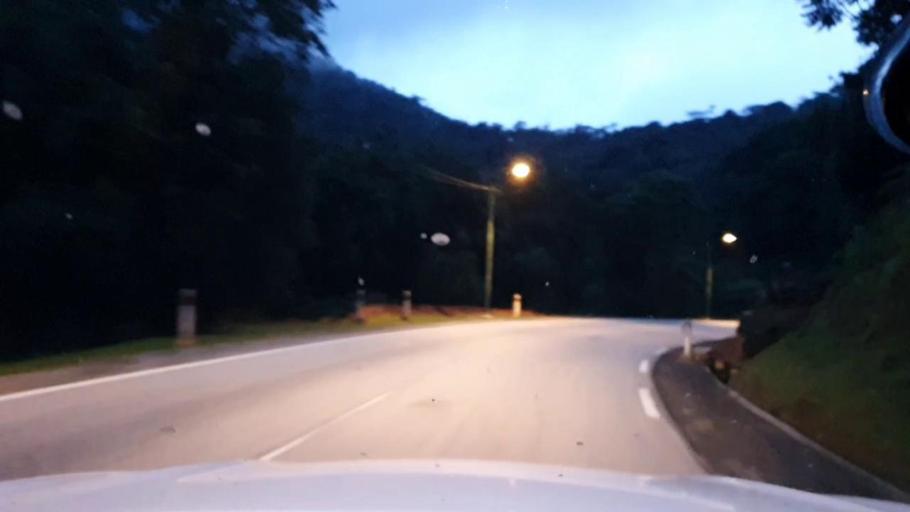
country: RW
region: Southern Province
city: Nzega
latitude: -2.5291
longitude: 29.3812
